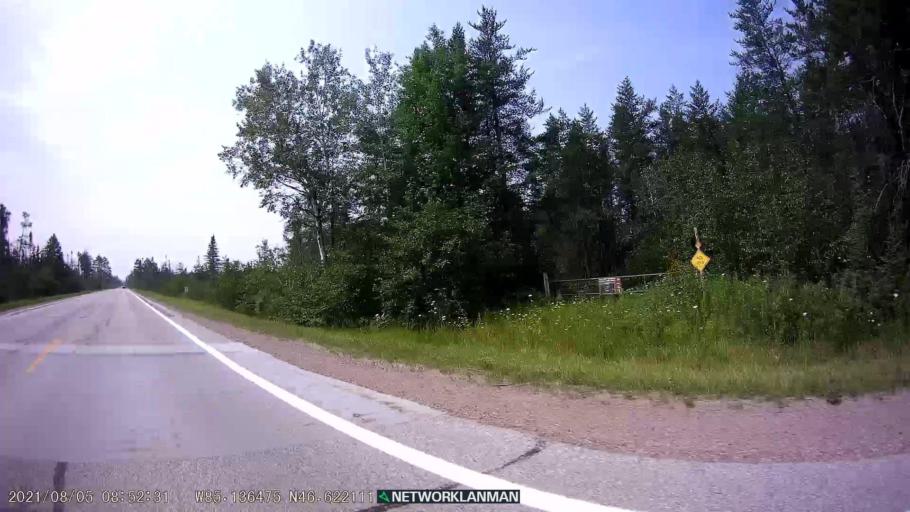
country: US
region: Michigan
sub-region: Luce County
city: Newberry
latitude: 46.6220
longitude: -85.1364
